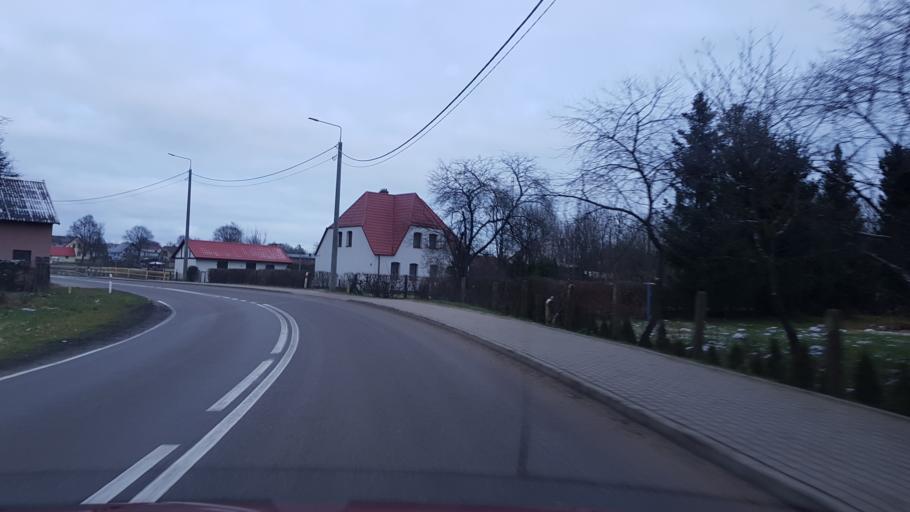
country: PL
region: Pomeranian Voivodeship
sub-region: Powiat czluchowski
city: Koczala
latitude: 54.0208
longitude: 17.1685
